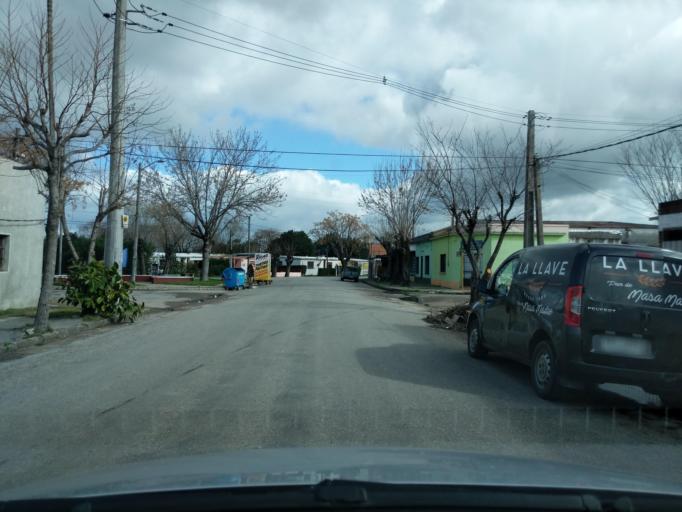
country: UY
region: Florida
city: Florida
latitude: -34.1071
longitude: -56.2119
